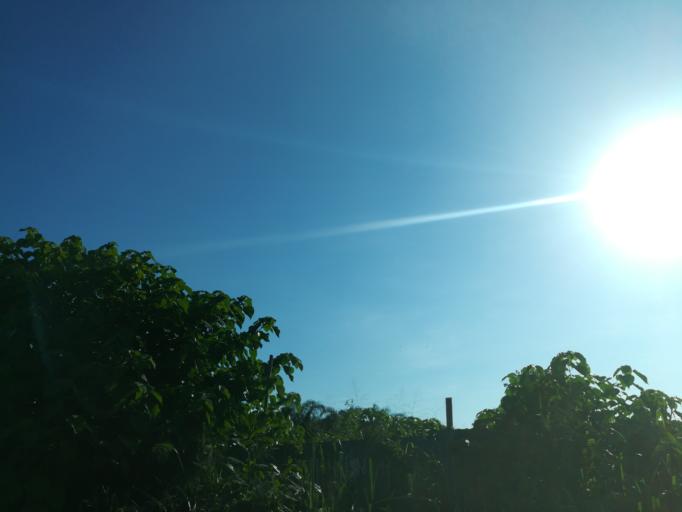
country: NG
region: Lagos
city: Ebute Ikorodu
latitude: 6.5503
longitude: 3.5409
